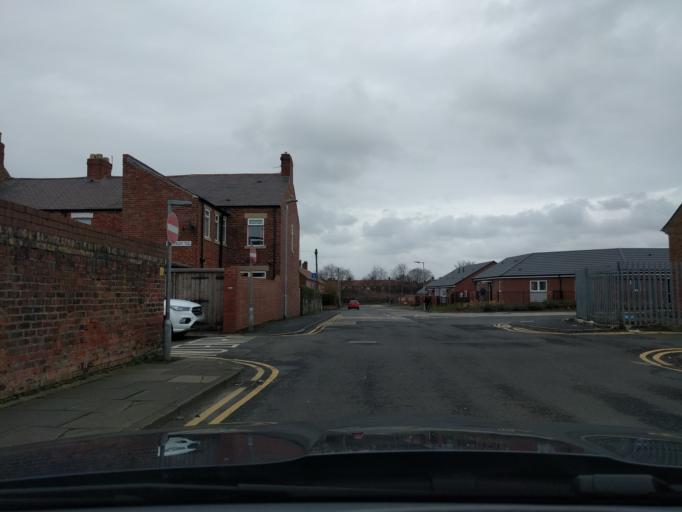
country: GB
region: England
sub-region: Northumberland
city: Ashington
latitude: 55.1796
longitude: -1.5683
